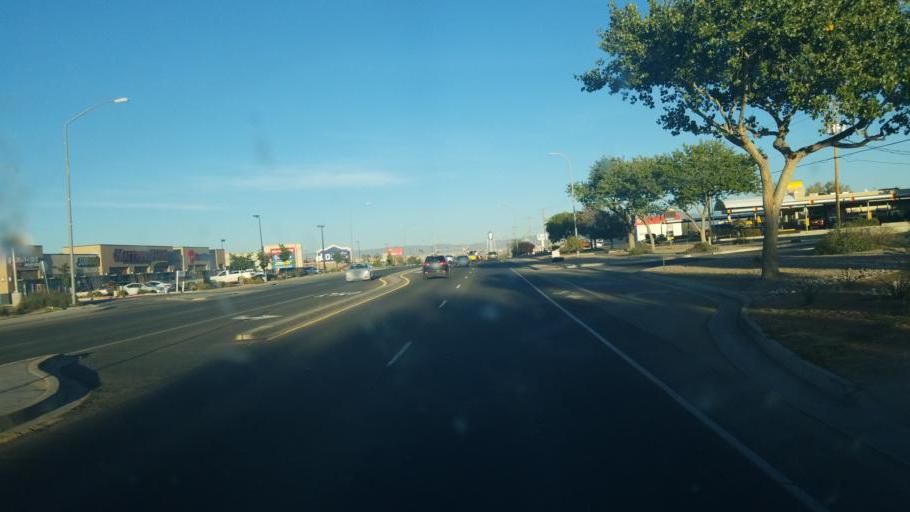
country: US
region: New Mexico
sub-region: Valencia County
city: Los Lunas
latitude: 34.8139
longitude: -106.7537
